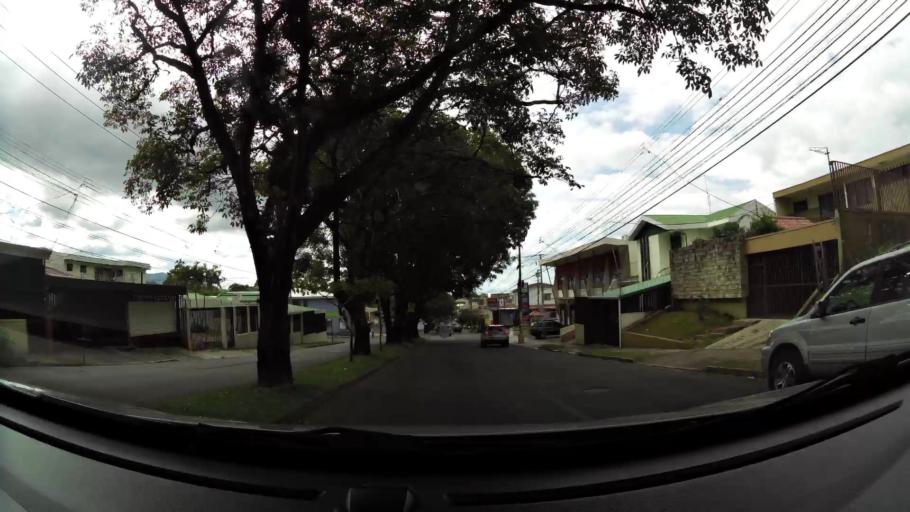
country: CR
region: San Jose
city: San Rafael
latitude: 9.9468
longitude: -84.1240
